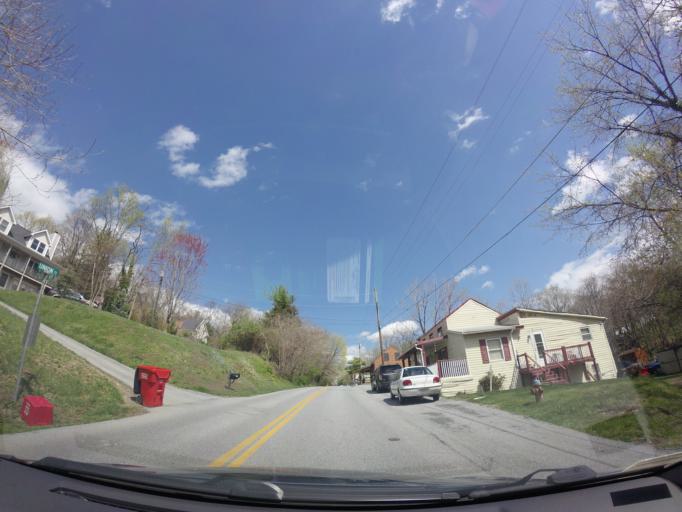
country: US
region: West Virginia
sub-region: Jefferson County
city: Bolivar
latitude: 39.3241
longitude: -77.7458
